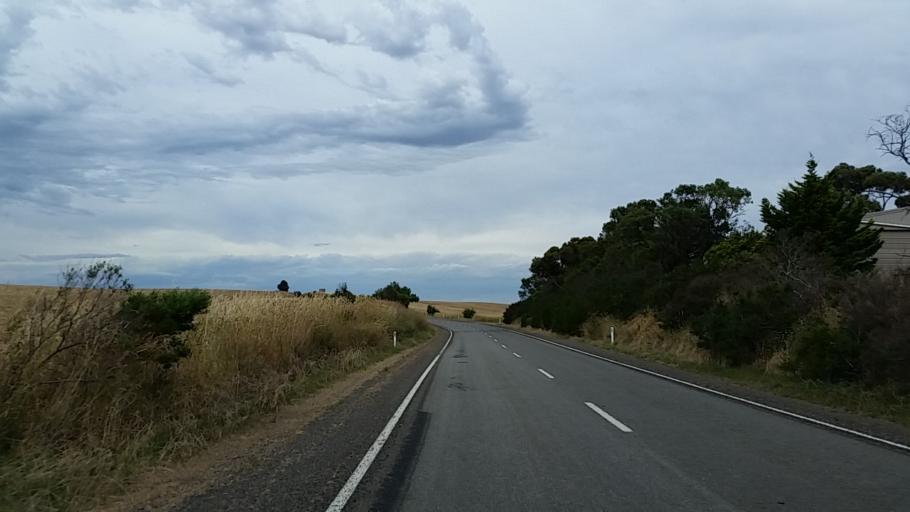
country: AU
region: South Australia
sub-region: Onkaparinga
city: Port Willunga
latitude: -35.3820
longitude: 138.4373
